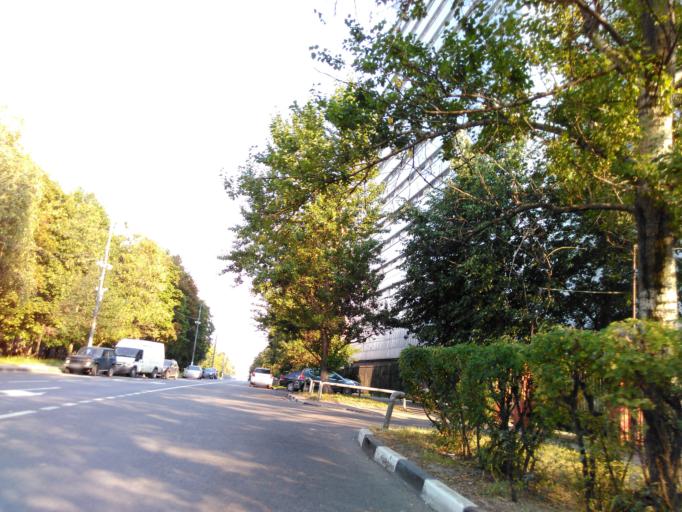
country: RU
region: Moskovskaya
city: Cheremushki
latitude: 55.6464
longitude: 37.5297
